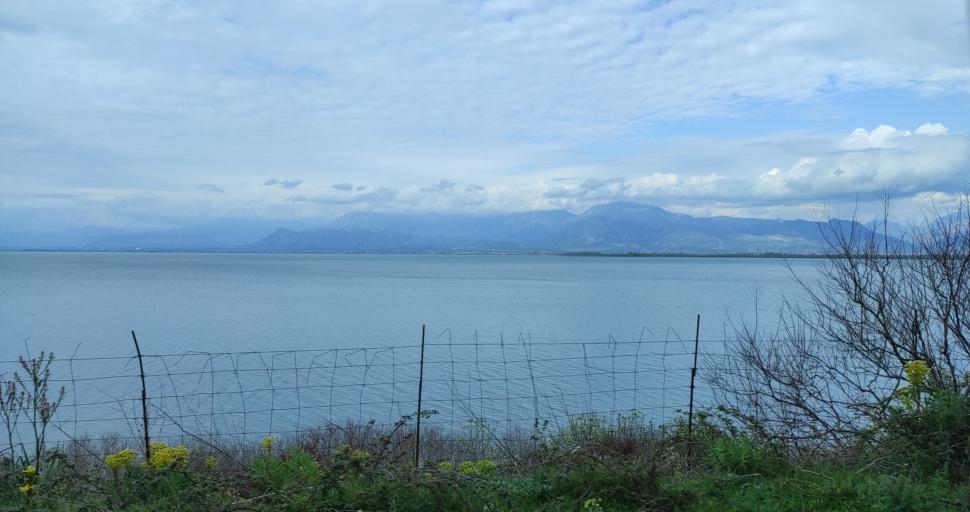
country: AL
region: Shkoder
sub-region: Rrethi i Shkodres
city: Berdica e Madhe
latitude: 42.0652
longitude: 19.4325
